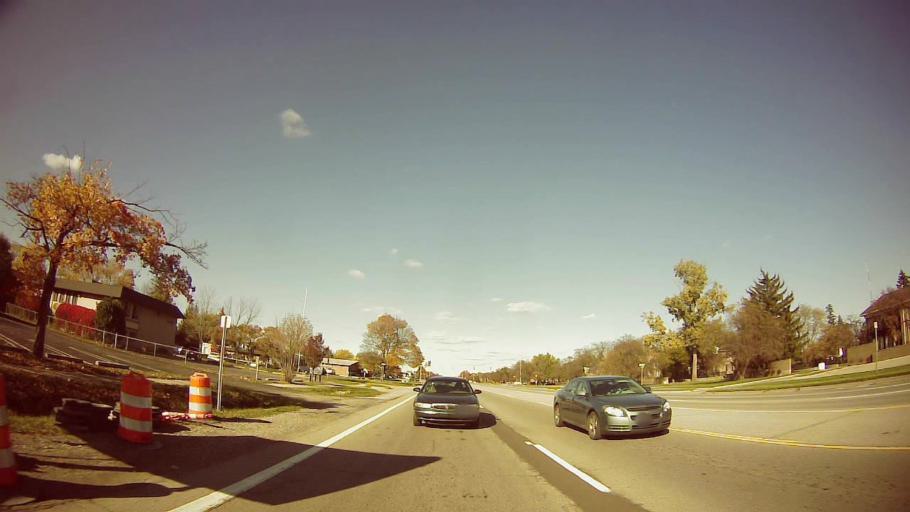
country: US
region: Michigan
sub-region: Oakland County
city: Southfield
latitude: 42.4755
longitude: -83.2213
